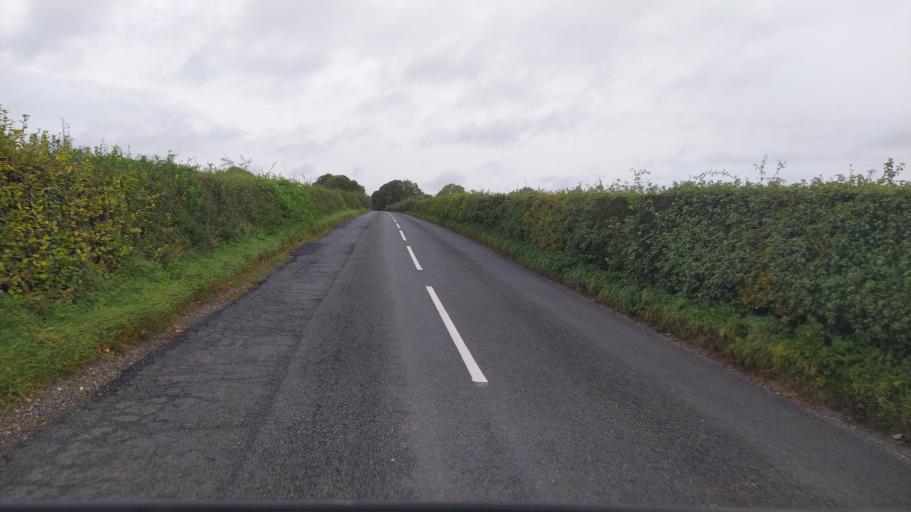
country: GB
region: England
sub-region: Hampshire
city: East Dean
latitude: 51.0809
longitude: -1.5596
